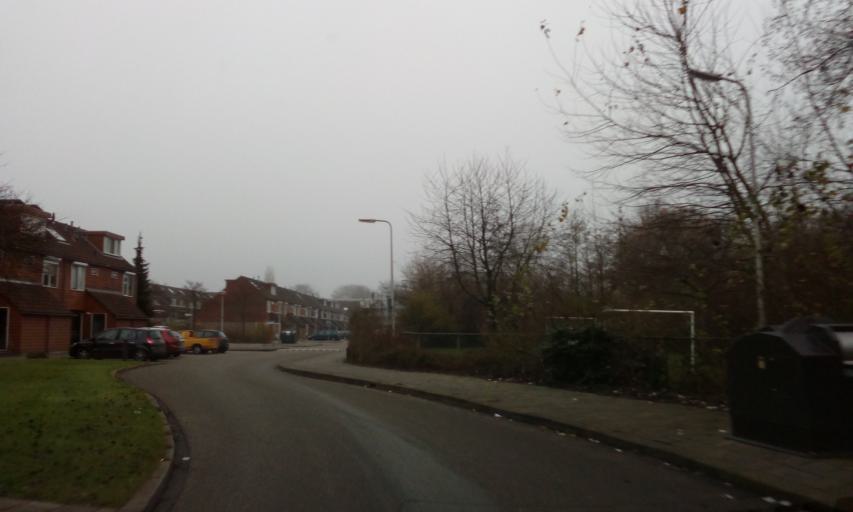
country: NL
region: South Holland
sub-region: Gemeente Krimpen aan den IJssel
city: Krimpen aan den IJssel
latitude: 51.9674
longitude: 4.6204
